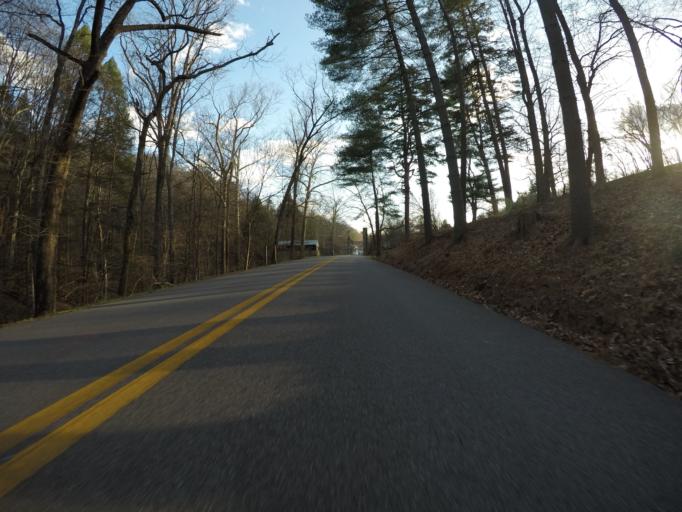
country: US
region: West Virginia
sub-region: Kanawha County
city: Charleston
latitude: 38.3779
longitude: -81.5827
